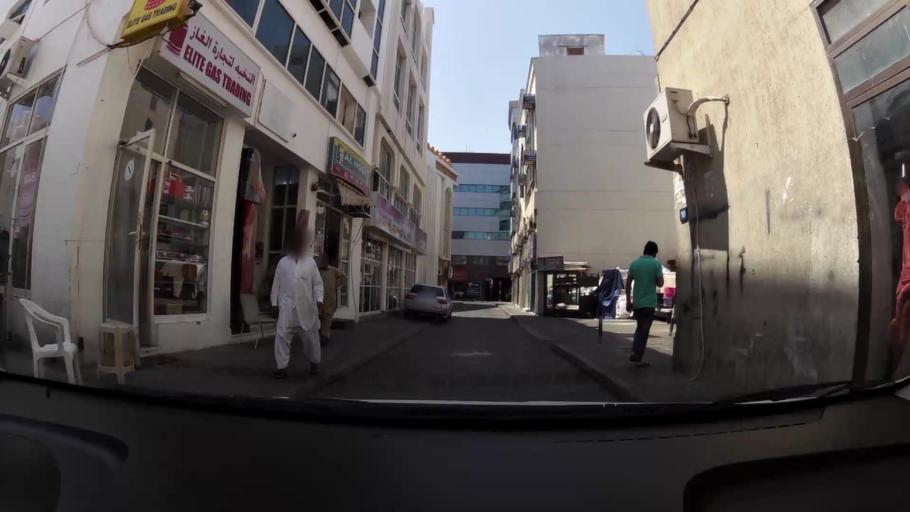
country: AE
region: Ash Shariqah
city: Sharjah
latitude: 25.2718
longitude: 55.3084
